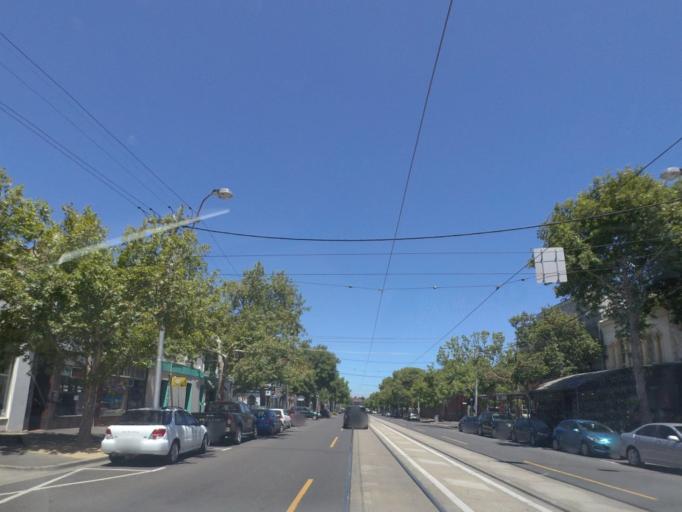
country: AU
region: Victoria
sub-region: Port Phillip
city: South Melbourne
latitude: -37.8358
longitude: 144.9619
